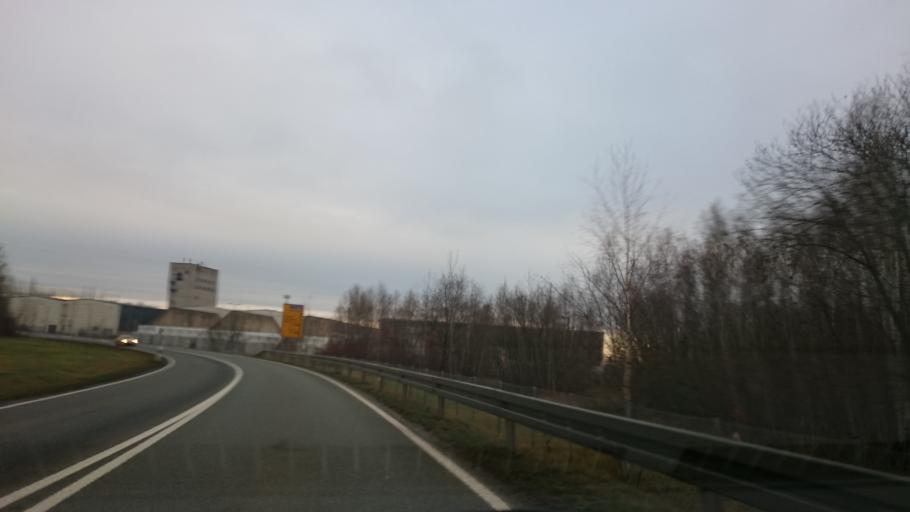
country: DE
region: Saxony
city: Mulsen
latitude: 50.7298
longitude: 12.5527
